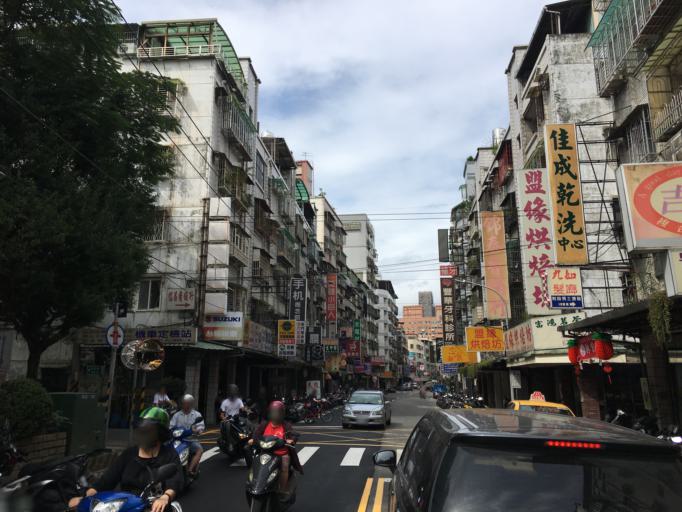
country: TW
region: Taipei
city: Taipei
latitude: 25.0885
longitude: 121.4741
